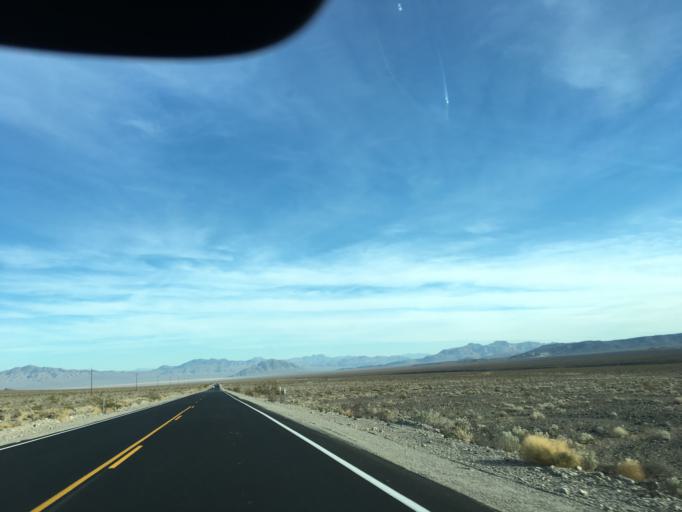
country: US
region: Nevada
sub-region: Nye County
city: Pahrump
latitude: 36.3222
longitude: -116.5570
